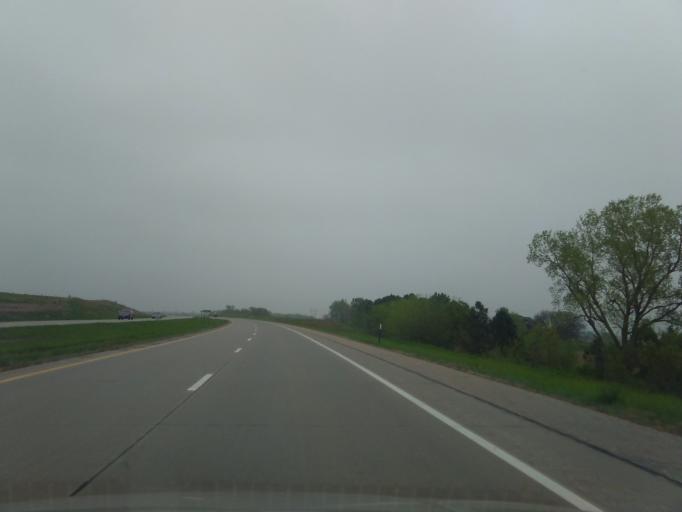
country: US
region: Nebraska
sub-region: Saunders County
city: Wahoo
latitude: 41.1012
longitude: -96.6336
